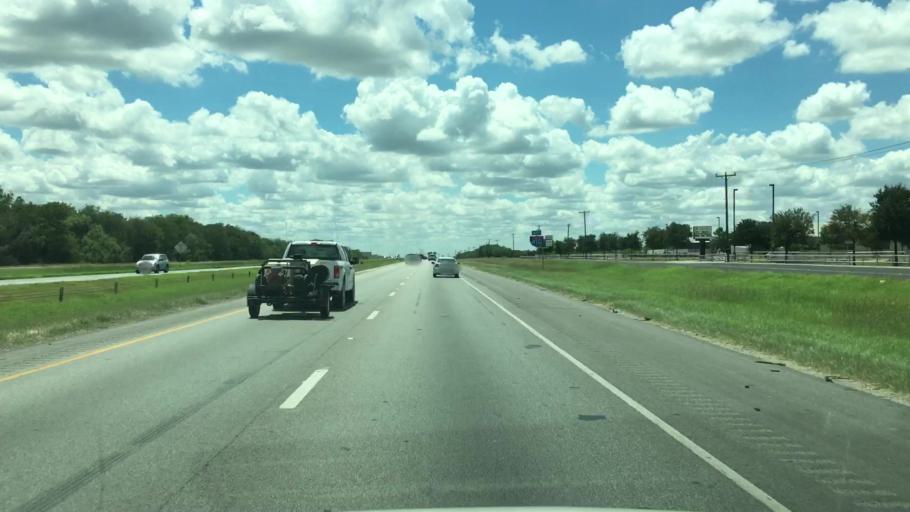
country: US
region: Texas
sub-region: Bexar County
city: China Grove
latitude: 29.3670
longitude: -98.3967
